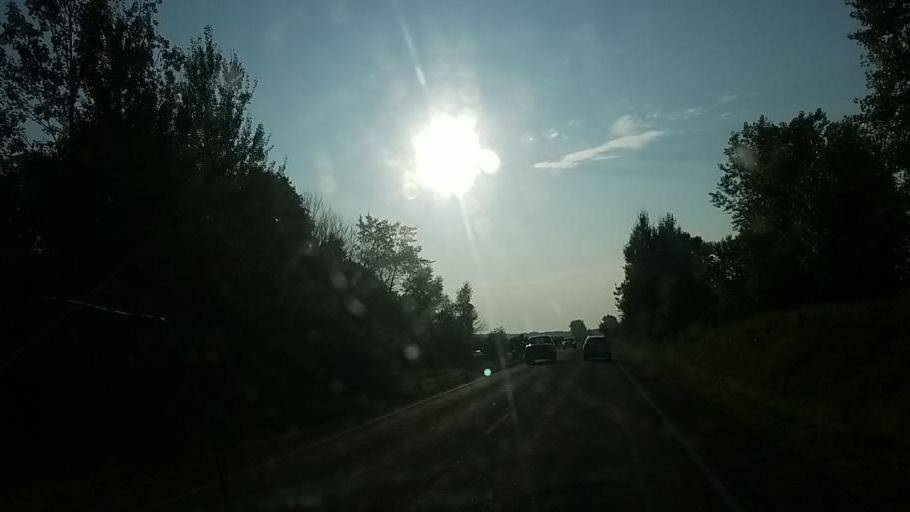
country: US
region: Michigan
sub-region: Montcalm County
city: Greenville
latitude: 43.2502
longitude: -85.1898
